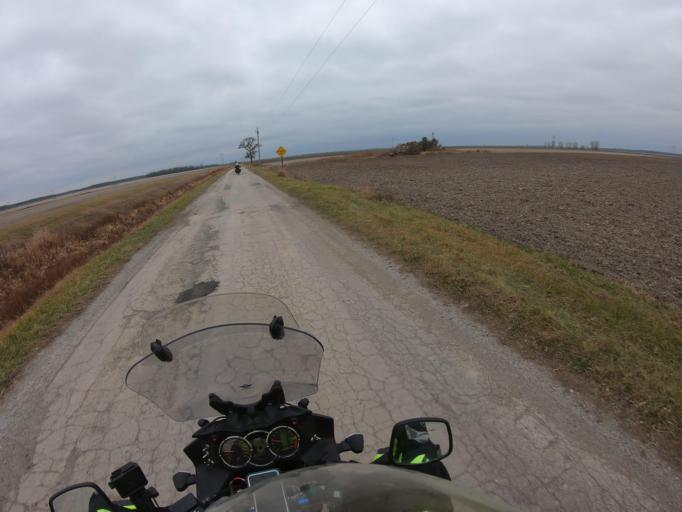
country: US
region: Michigan
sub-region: Saginaw County
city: Burt
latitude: 43.2637
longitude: -83.9750
